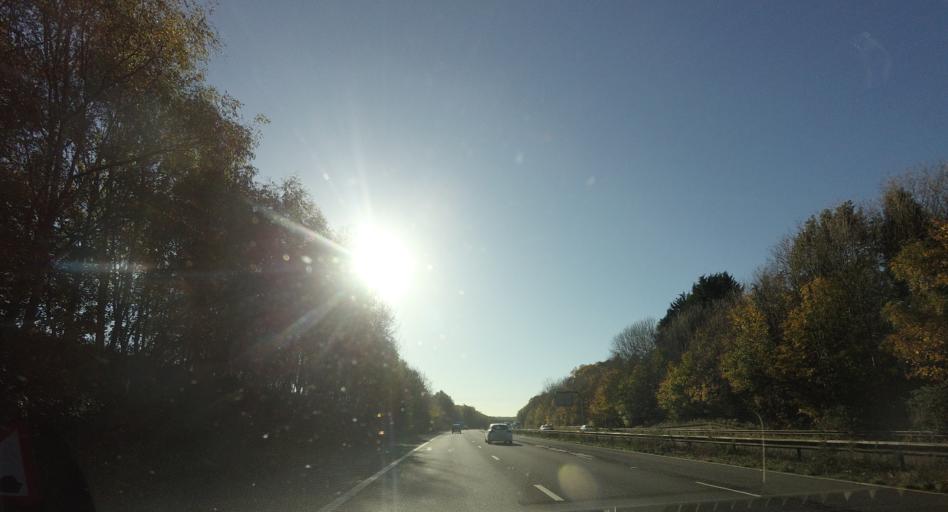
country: GB
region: England
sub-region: West Sussex
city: Maidenbower
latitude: 51.1155
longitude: -0.1371
